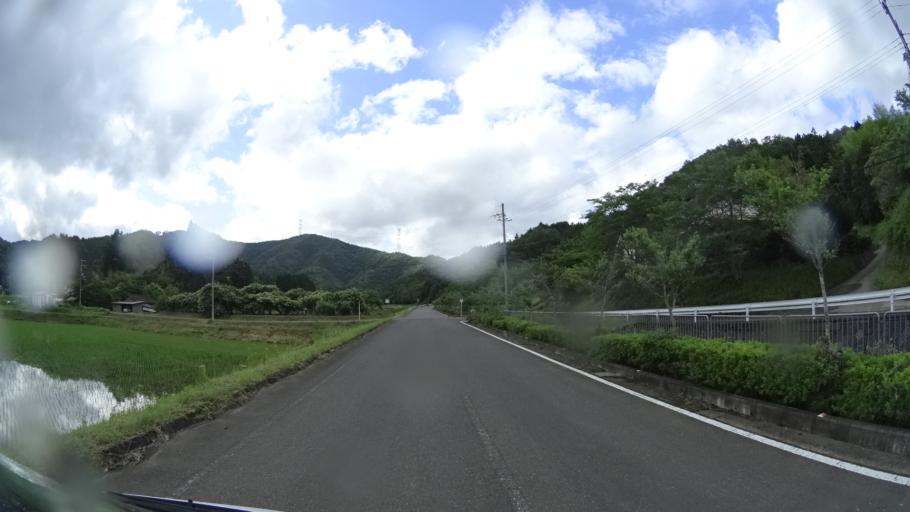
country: JP
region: Kyoto
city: Ayabe
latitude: 35.3482
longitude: 135.1985
